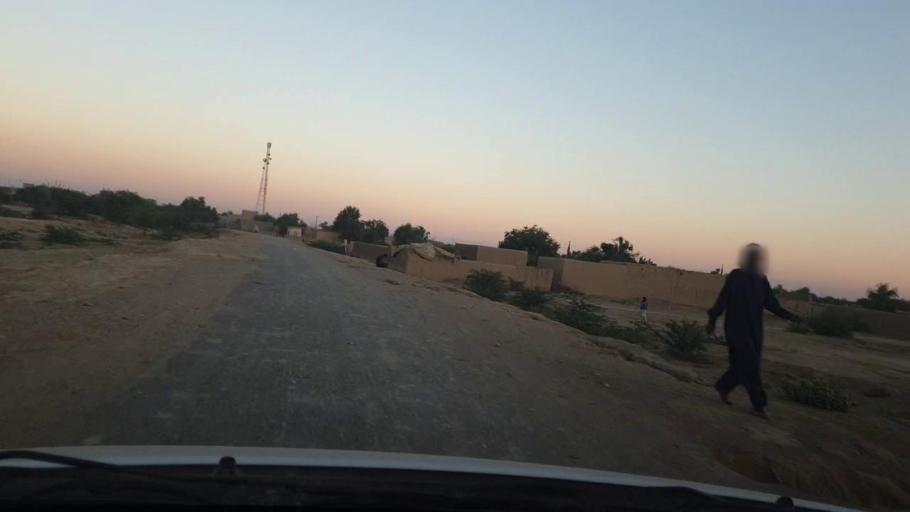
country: PK
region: Sindh
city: Johi
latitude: 26.8287
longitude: 67.4712
